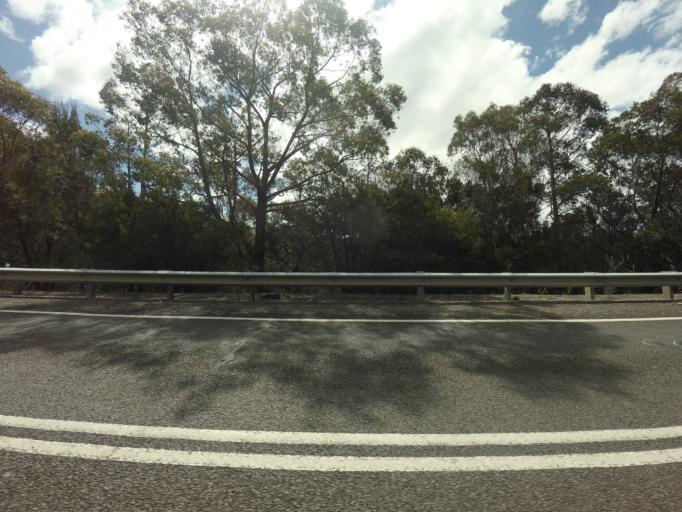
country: AU
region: Tasmania
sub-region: Break O'Day
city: St Helens
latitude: -42.0145
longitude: 147.9195
